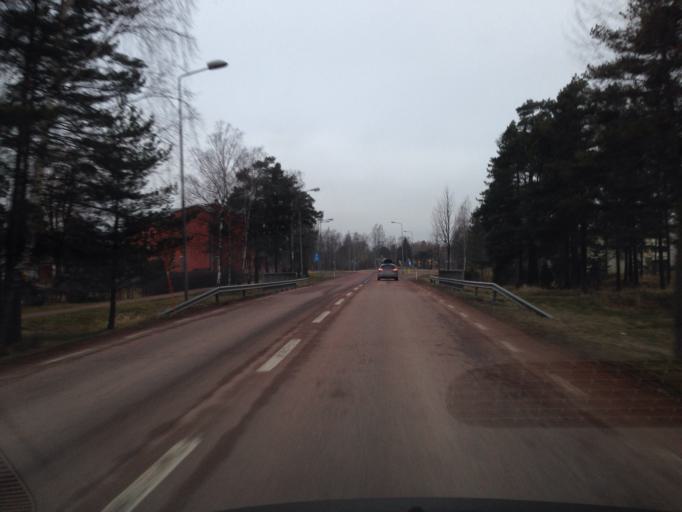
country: AX
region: Mariehamns stad
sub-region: Mariehamn
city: Mariehamn
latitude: 60.1058
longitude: 19.9345
